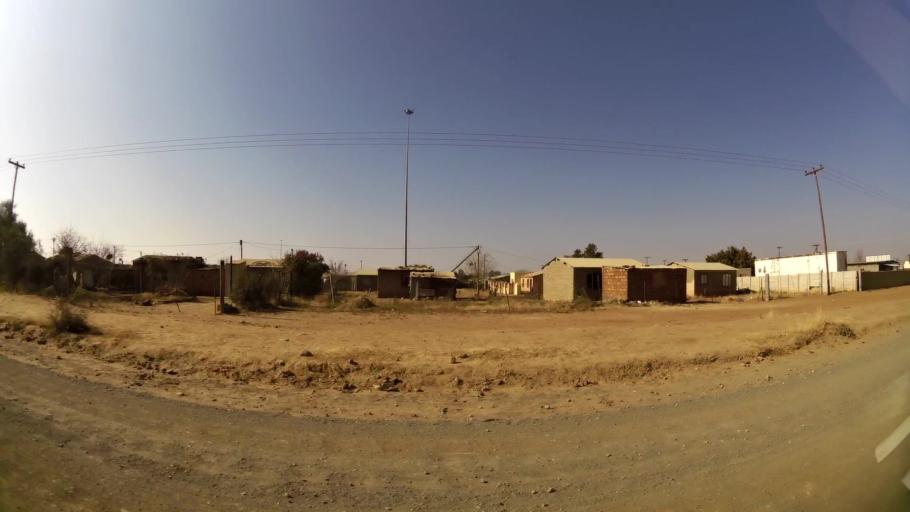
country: ZA
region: Orange Free State
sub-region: Mangaung Metropolitan Municipality
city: Bloemfontein
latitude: -29.1896
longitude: 26.2837
